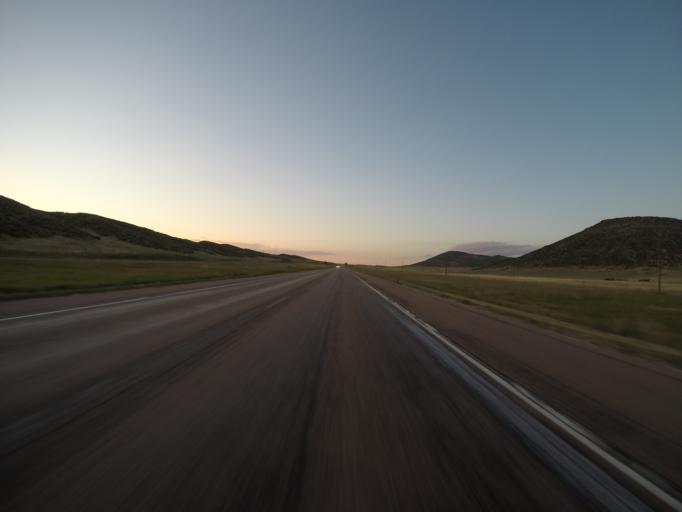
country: US
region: Colorado
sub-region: Larimer County
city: Laporte
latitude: 40.7342
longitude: -105.1711
